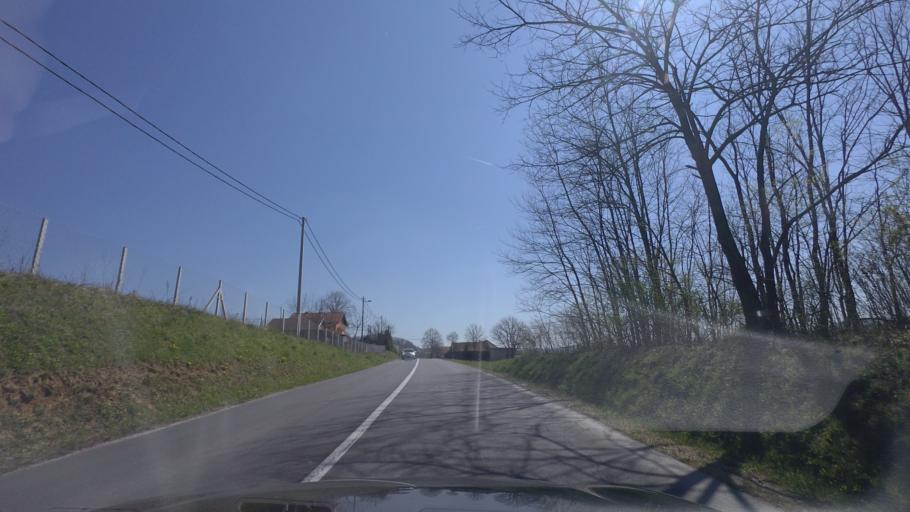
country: HR
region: Karlovacka
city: Vojnic
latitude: 45.3437
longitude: 15.6848
